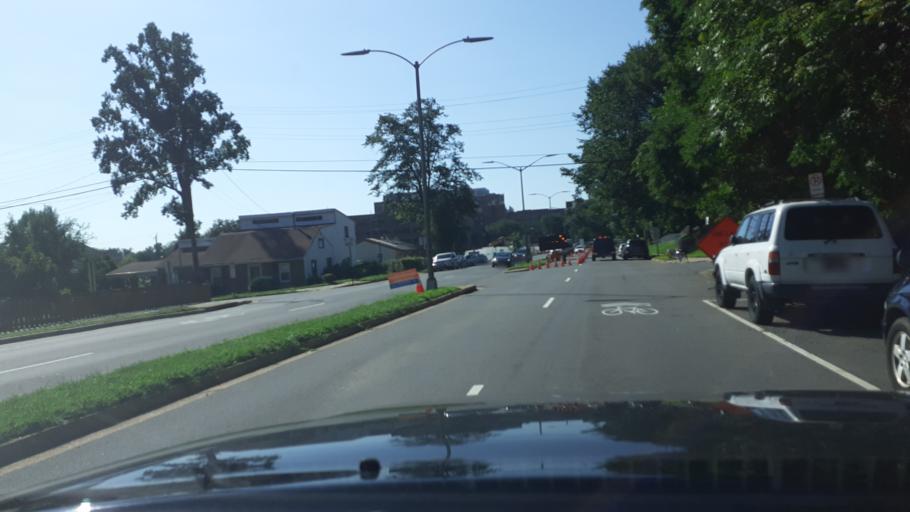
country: US
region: Virginia
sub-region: Arlington County
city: Arlington
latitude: 38.8923
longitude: -77.1304
